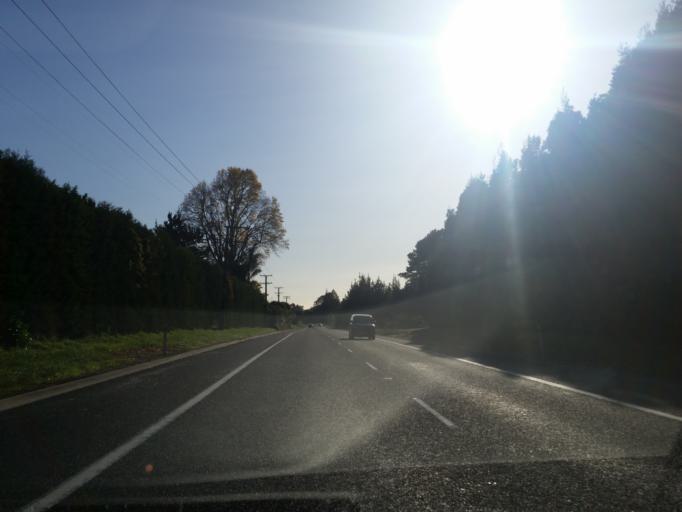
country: NZ
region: Bay of Plenty
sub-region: Western Bay of Plenty District
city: Katikati
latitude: -37.5052
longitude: 175.9232
